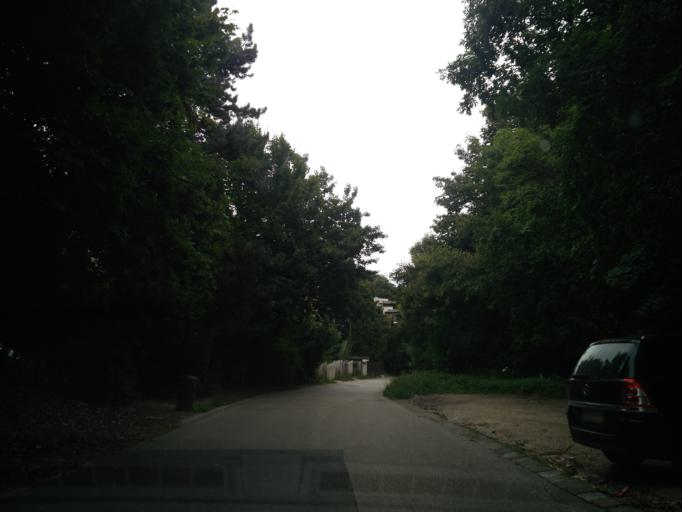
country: HU
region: Budapest
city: Budapest XII. keruelet
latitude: 47.5071
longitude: 18.9906
